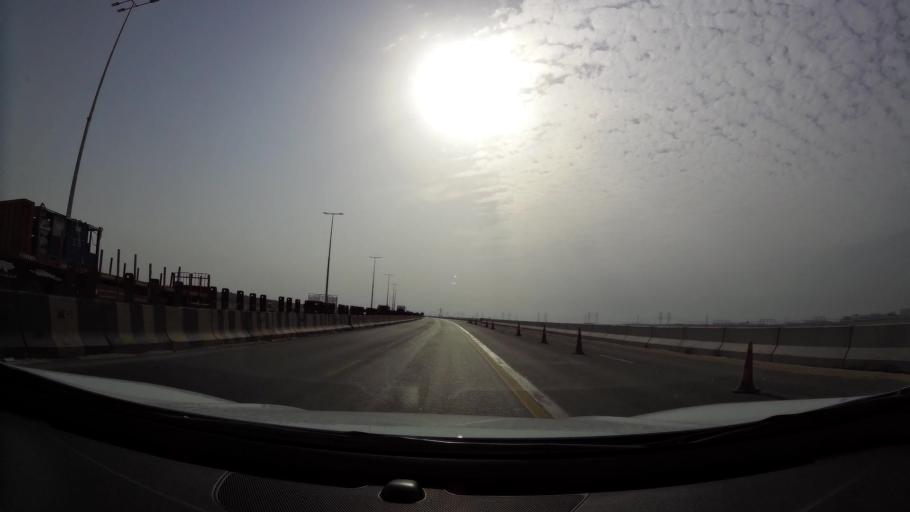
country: AE
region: Abu Dhabi
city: Abu Dhabi
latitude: 24.2694
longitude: 54.4992
